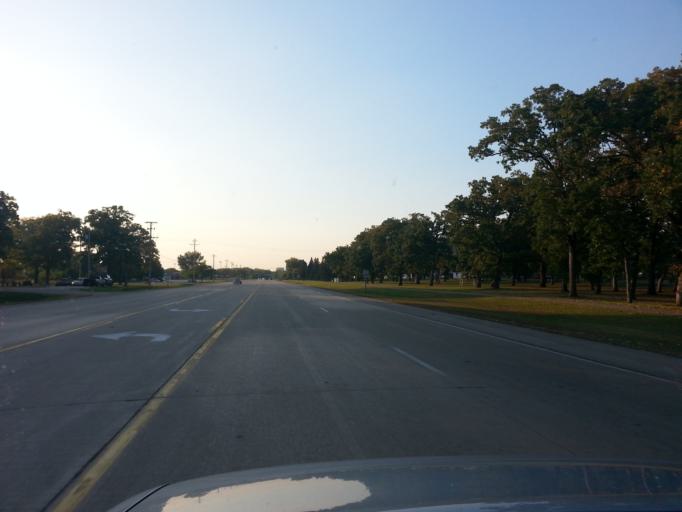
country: US
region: Minnesota
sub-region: Olmsted County
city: Rochester
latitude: 43.9957
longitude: -92.4272
